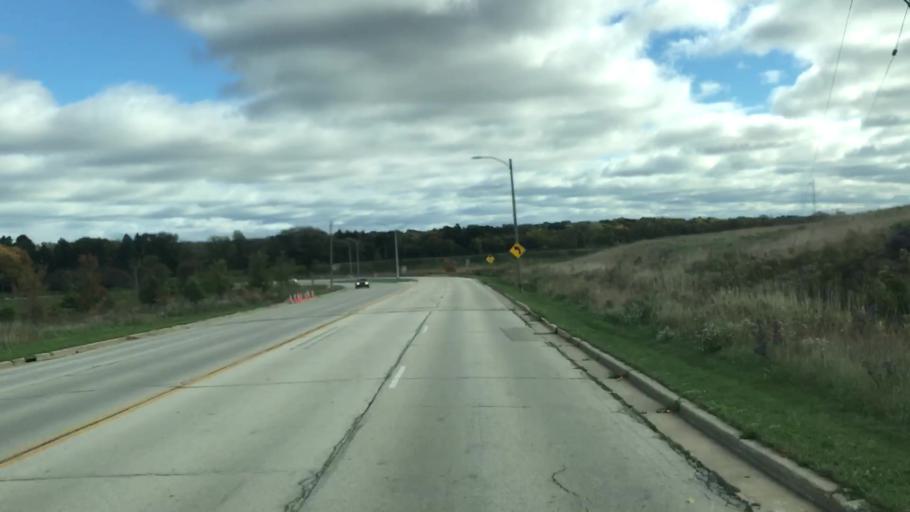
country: US
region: Wisconsin
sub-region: Milwaukee County
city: Wauwatosa
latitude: 43.0524
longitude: -88.0318
